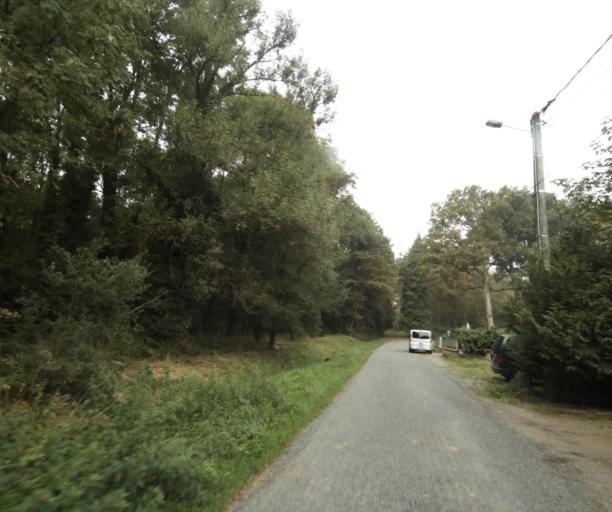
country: FR
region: Bourgogne
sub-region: Departement de Saone-et-Loire
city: Charolles
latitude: 46.4395
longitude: 4.2610
